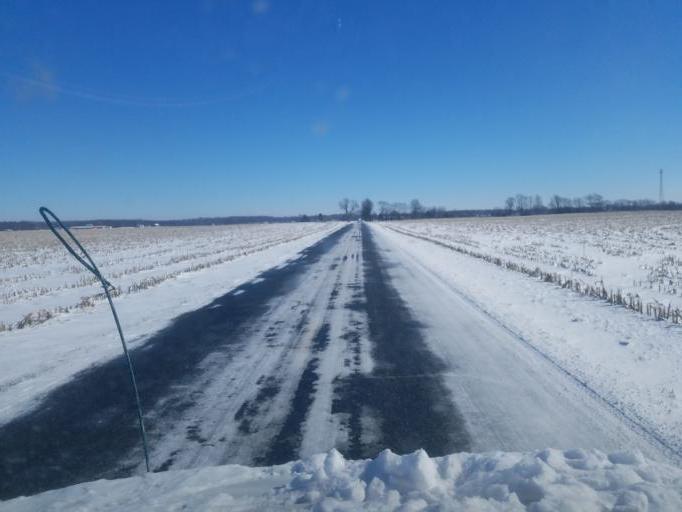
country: US
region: Ohio
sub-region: Delaware County
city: Delaware
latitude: 40.2877
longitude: -83.0034
